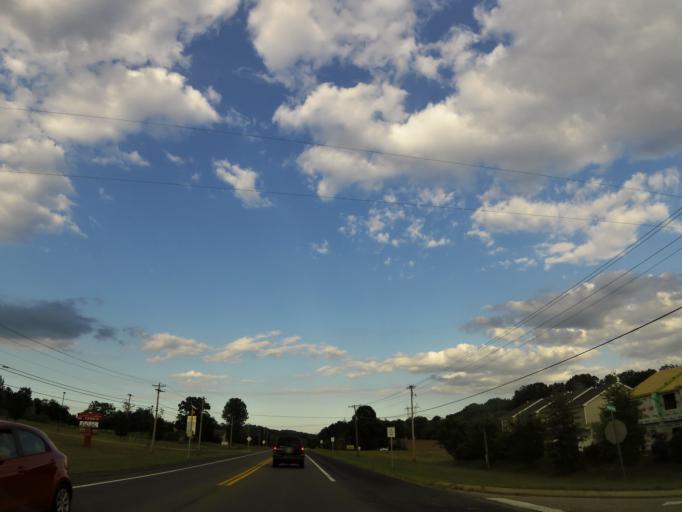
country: US
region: Tennessee
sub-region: Maury County
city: Columbia
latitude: 35.6363
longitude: -86.9696
